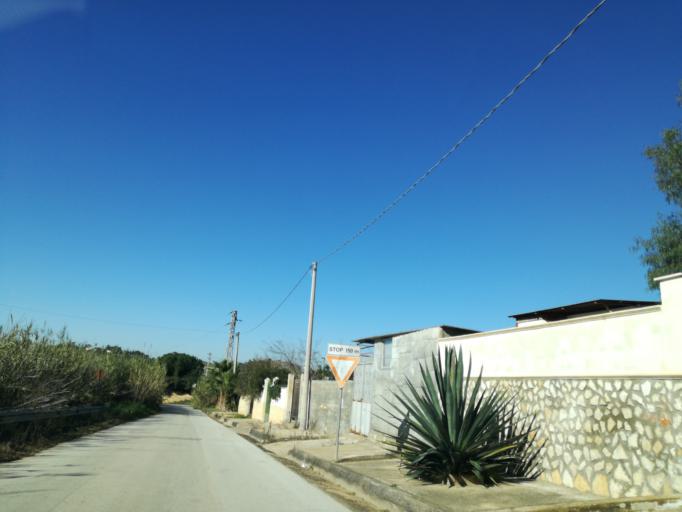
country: IT
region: Sicily
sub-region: Provincia di Caltanissetta
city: Niscemi
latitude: 37.0618
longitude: 14.3428
